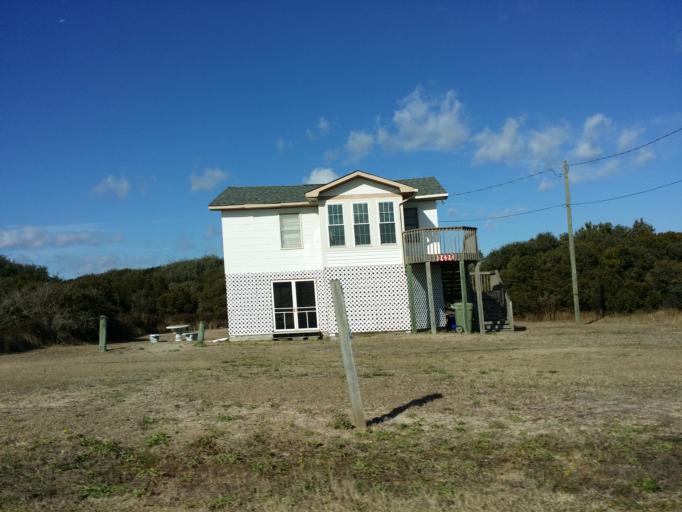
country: US
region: North Carolina
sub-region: Pender County
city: Surf City
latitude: 34.4552
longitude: -77.4968
